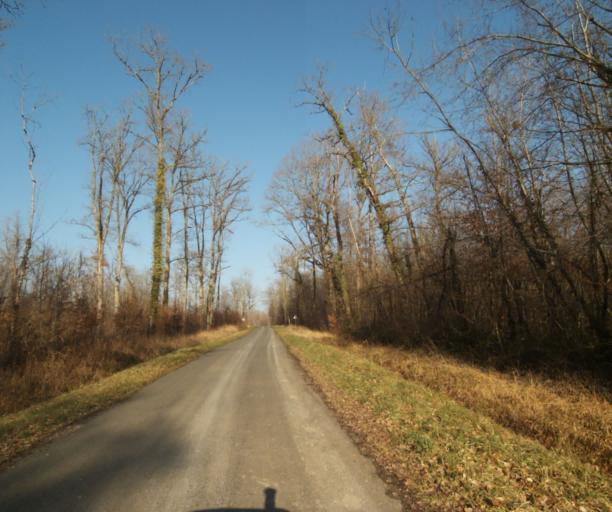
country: FR
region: Champagne-Ardenne
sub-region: Departement de la Haute-Marne
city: Wassy
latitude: 48.4569
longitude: 4.9381
